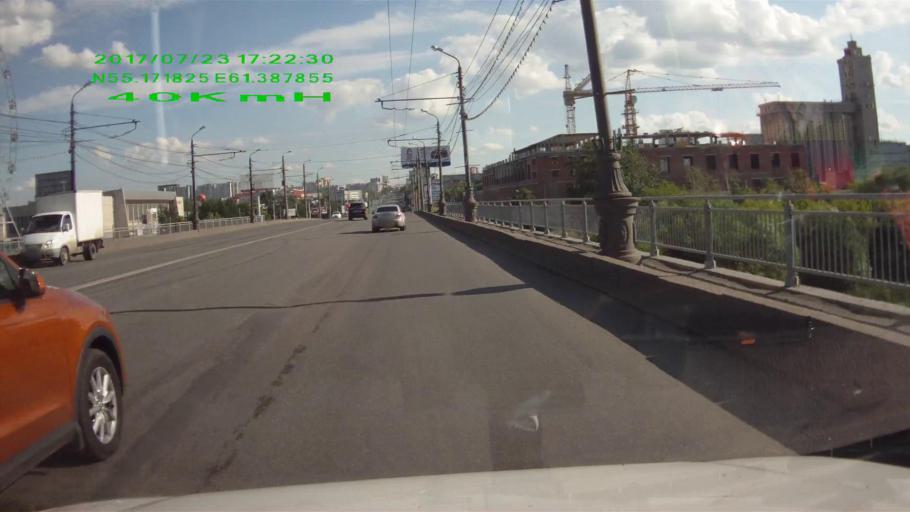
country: RU
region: Chelyabinsk
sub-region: Gorod Chelyabinsk
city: Chelyabinsk
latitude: 55.1714
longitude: 61.3879
